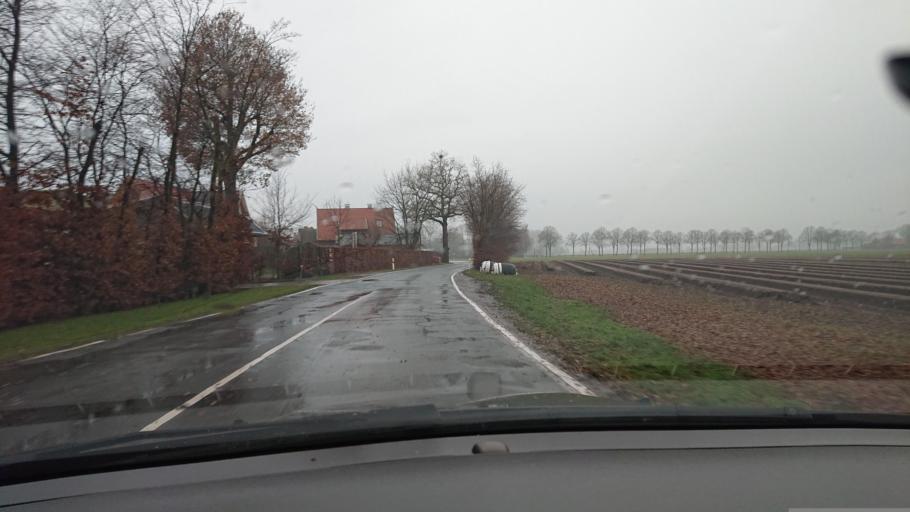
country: DE
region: North Rhine-Westphalia
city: Oelde
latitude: 51.8617
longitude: 8.2051
